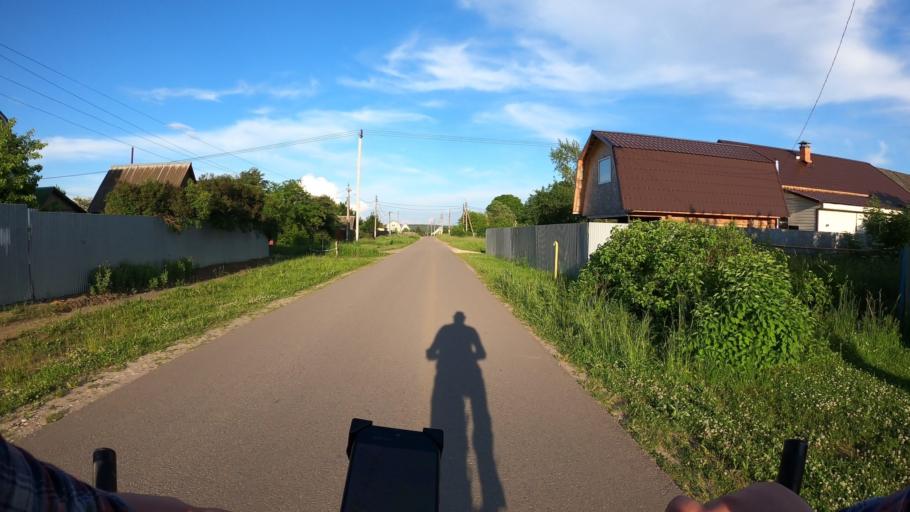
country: RU
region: Moskovskaya
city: Ashitkovo
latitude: 55.4546
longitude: 38.5893
